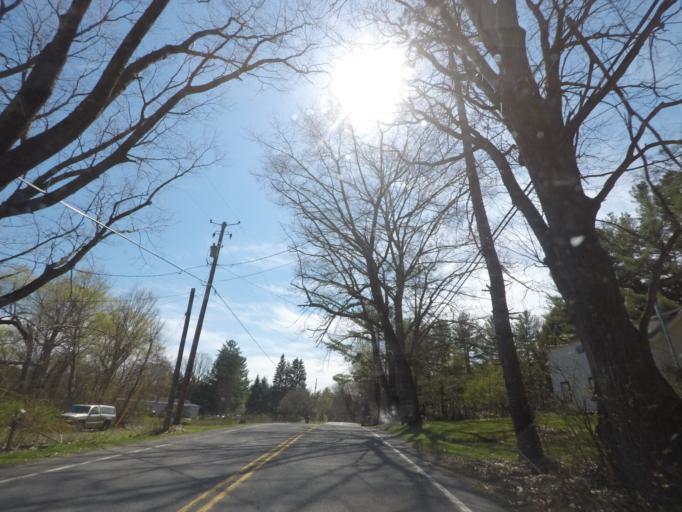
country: US
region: New York
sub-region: Rensselaer County
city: Nassau
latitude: 42.4773
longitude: -73.4712
